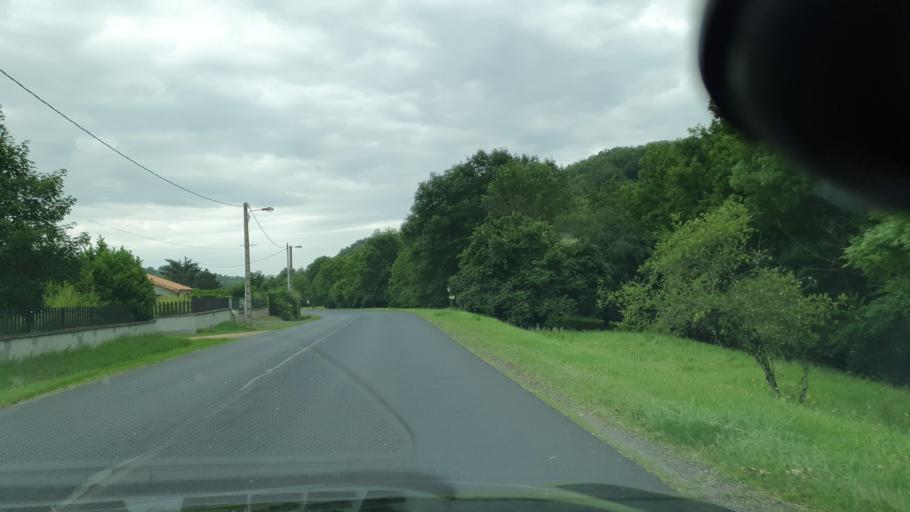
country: FR
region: Auvergne
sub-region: Departement du Puy-de-Dome
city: Champeix
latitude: 45.5884
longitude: 3.1110
